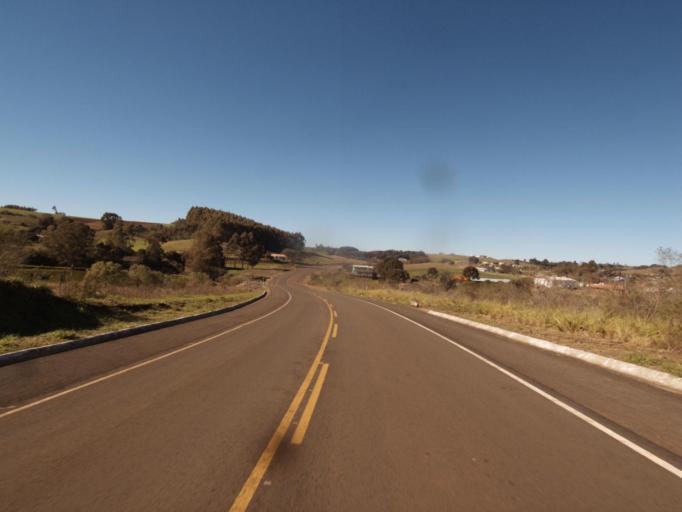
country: AR
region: Misiones
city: Bernardo de Irigoyen
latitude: -26.6141
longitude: -53.6846
